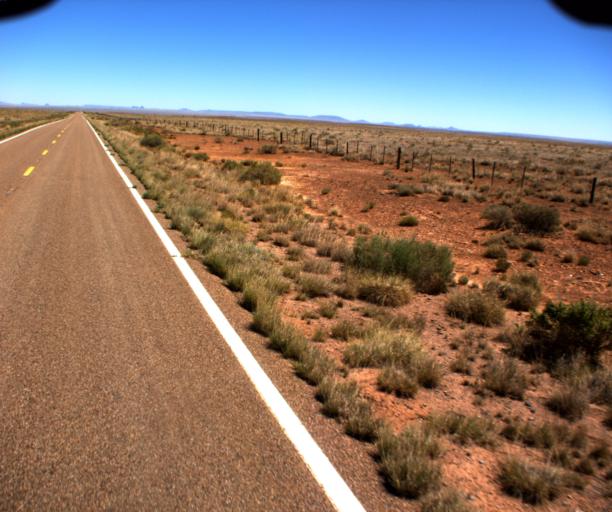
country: US
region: Arizona
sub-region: Navajo County
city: Winslow
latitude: 34.8830
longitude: -110.6512
